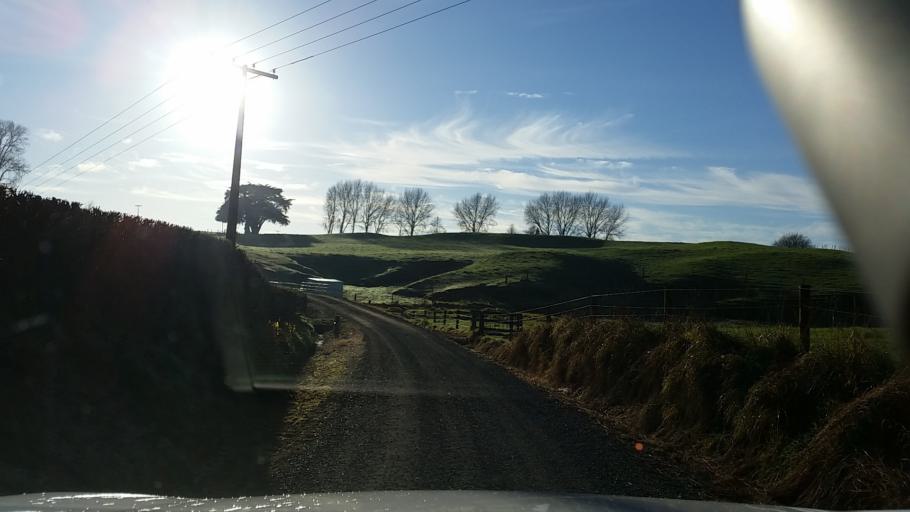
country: NZ
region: Waikato
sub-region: Matamata-Piako District
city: Matamata
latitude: -37.7268
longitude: 175.6348
